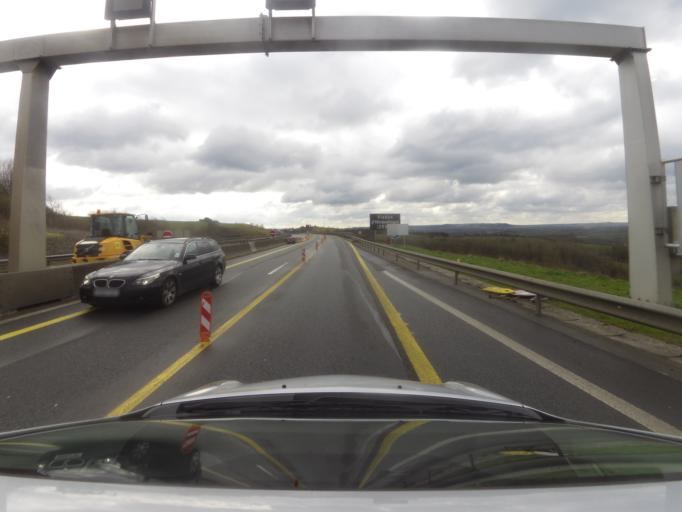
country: FR
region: Nord-Pas-de-Calais
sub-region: Departement du Pas-de-Calais
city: Isques
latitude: 50.6863
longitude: 1.6445
